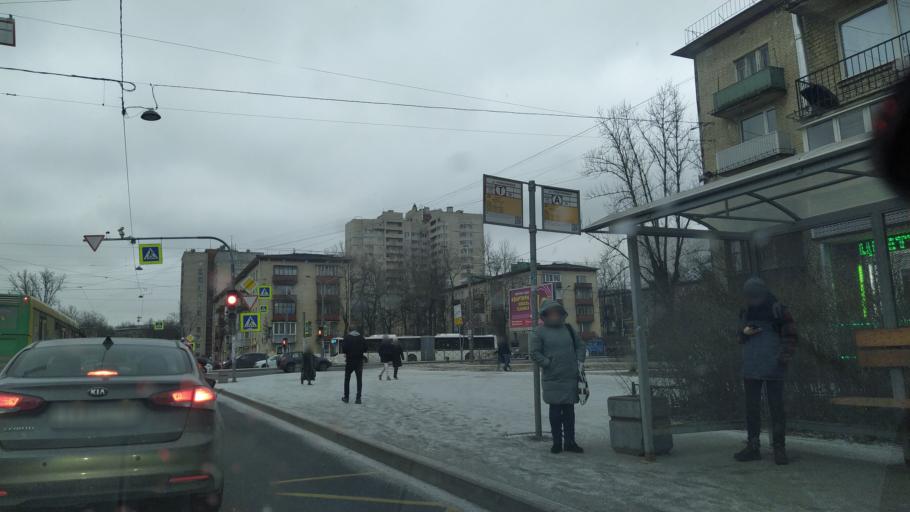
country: RU
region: St.-Petersburg
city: Kupchino
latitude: 59.8450
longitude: 30.3301
